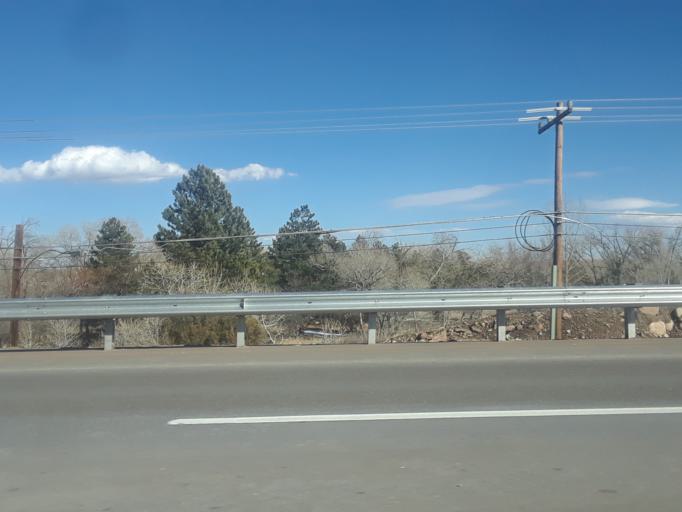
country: US
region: Colorado
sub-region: Boulder County
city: Lyons
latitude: 40.1294
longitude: -105.2823
